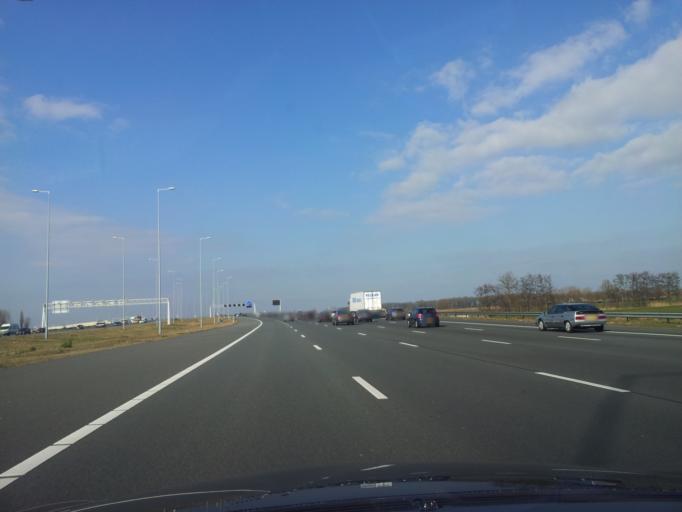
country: NL
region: Utrecht
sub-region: Stichtse Vecht
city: Breukelen
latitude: 52.2171
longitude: 4.9870
